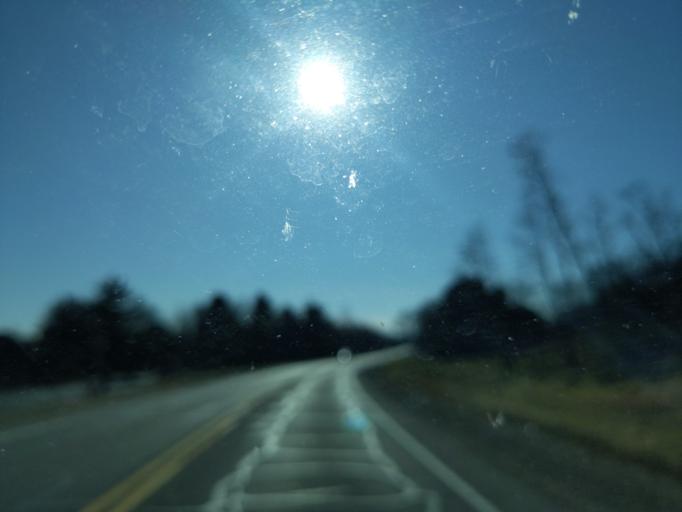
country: US
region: Wisconsin
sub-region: Waushara County
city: Wautoma
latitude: 44.0831
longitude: -89.2902
